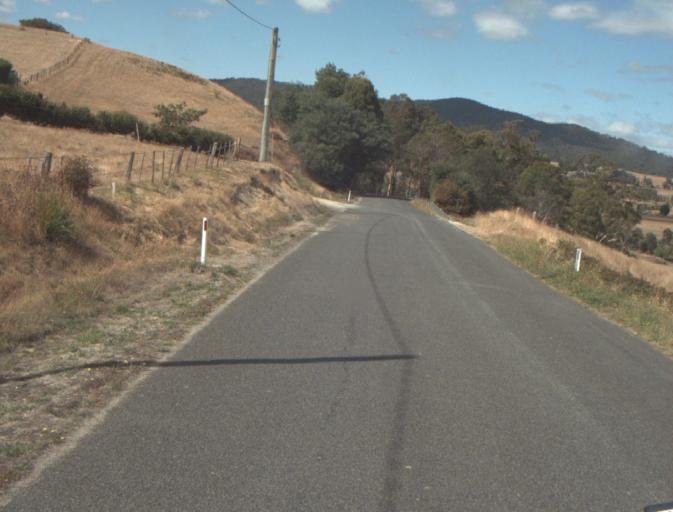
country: AU
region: Tasmania
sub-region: Launceston
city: Mayfield
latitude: -41.2381
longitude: 147.1484
